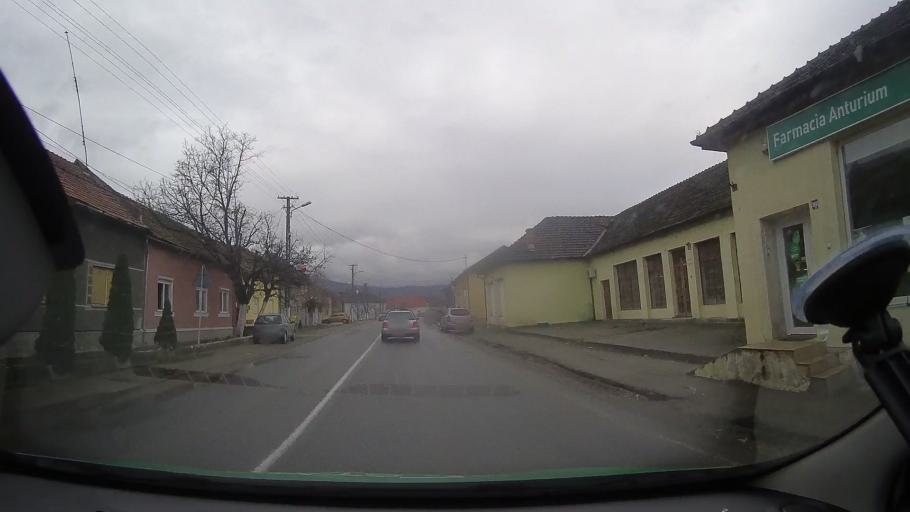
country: RO
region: Arad
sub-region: Comuna Buteni
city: Buteni
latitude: 46.3270
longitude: 22.1234
